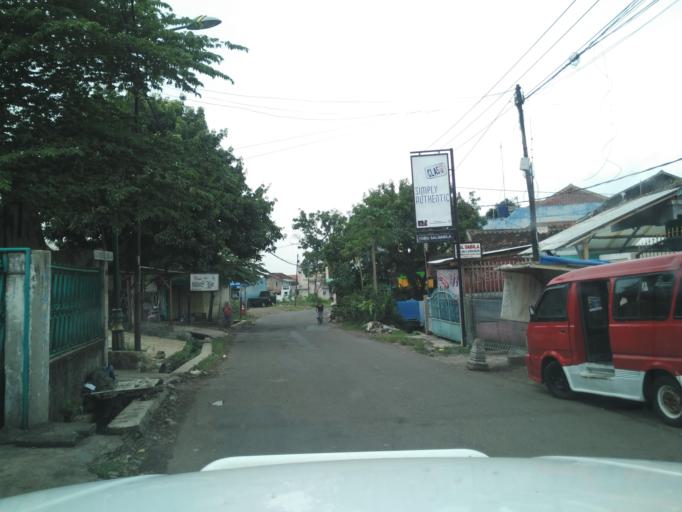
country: ID
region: West Java
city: Ciranjang-hilir
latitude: -6.8213
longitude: 107.1493
